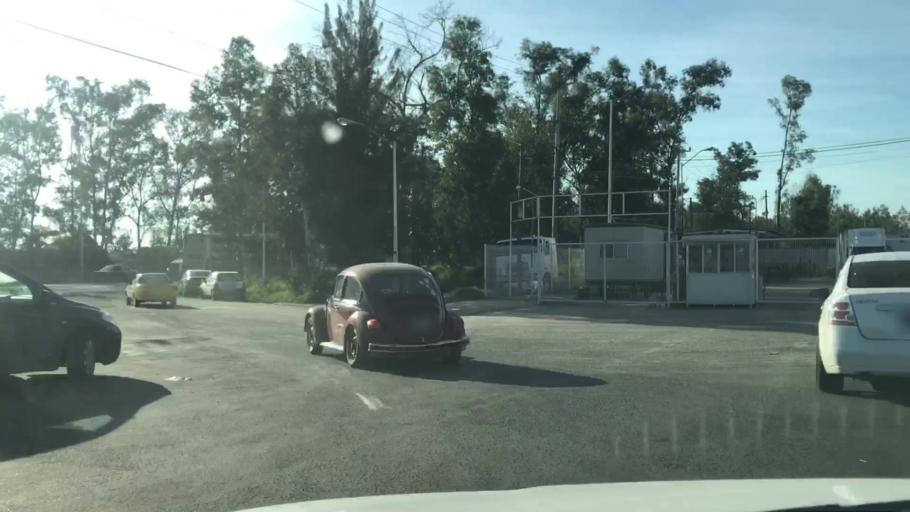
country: MX
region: Jalisco
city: Zapopan2
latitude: 20.6880
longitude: -103.4559
